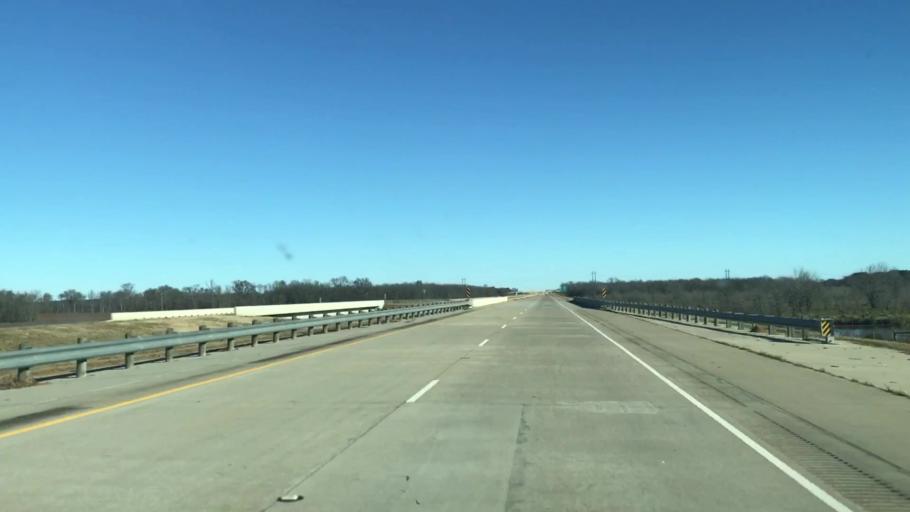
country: US
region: Louisiana
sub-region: Caddo Parish
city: Vivian
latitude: 32.8283
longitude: -93.8759
